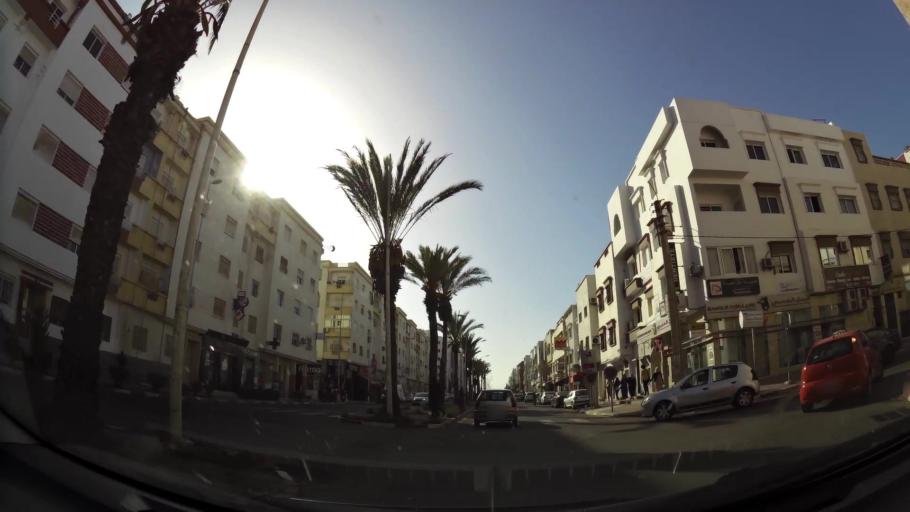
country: MA
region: Oued ed Dahab-Lagouira
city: Dakhla
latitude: 30.3995
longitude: -9.5517
